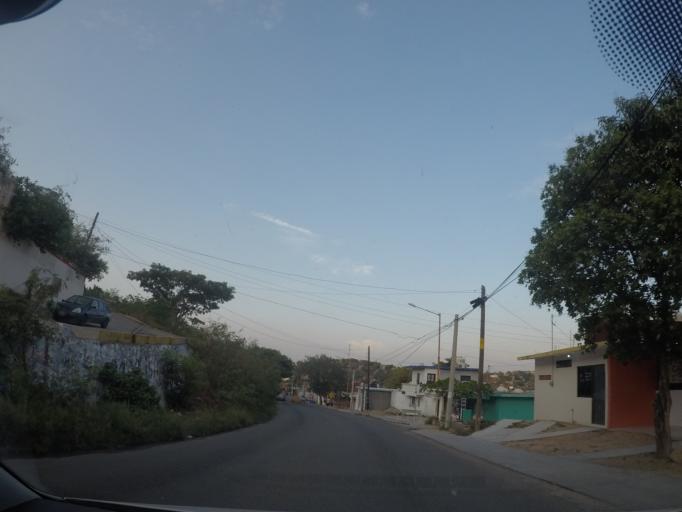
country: MX
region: Oaxaca
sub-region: Salina Cruz
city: Salina Cruz
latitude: 16.1931
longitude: -95.2071
